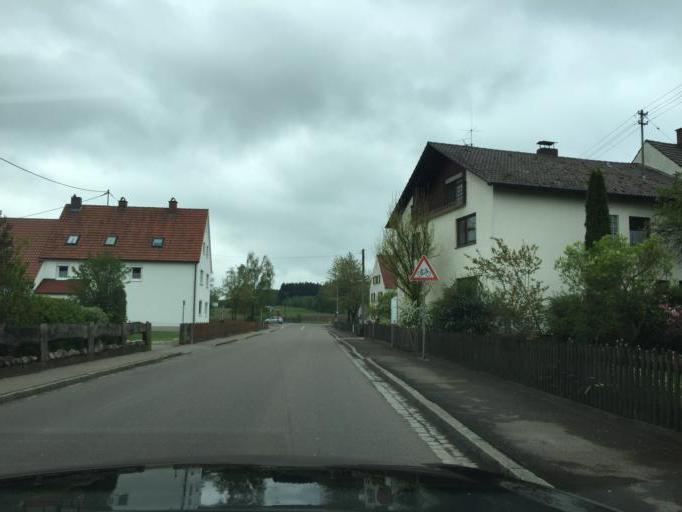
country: DE
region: Bavaria
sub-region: Swabia
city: Buttenwiesen
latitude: 48.5811
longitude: 10.7141
